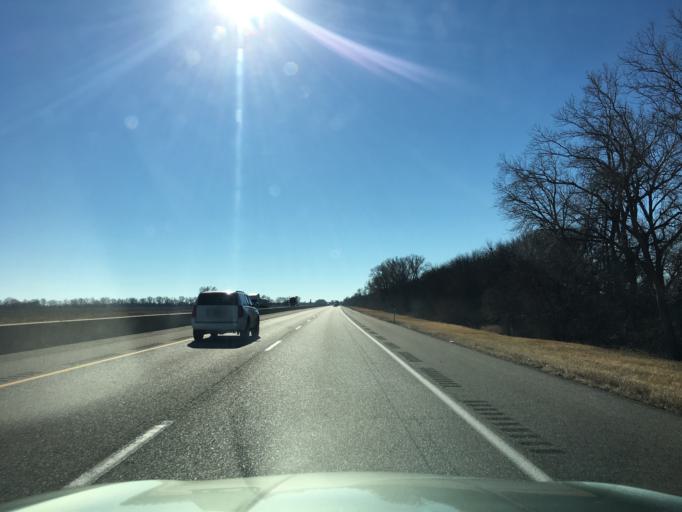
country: US
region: Kansas
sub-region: Sumner County
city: Belle Plaine
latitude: 37.4357
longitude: -97.3215
